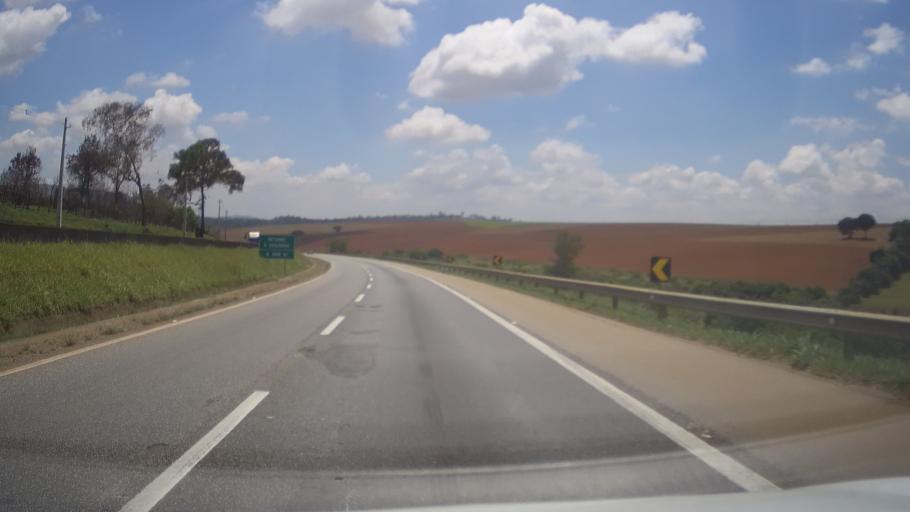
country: BR
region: Minas Gerais
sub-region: Sao Goncalo Do Sapucai
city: Sao Goncalo do Sapucai
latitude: -21.9367
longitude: -45.6136
